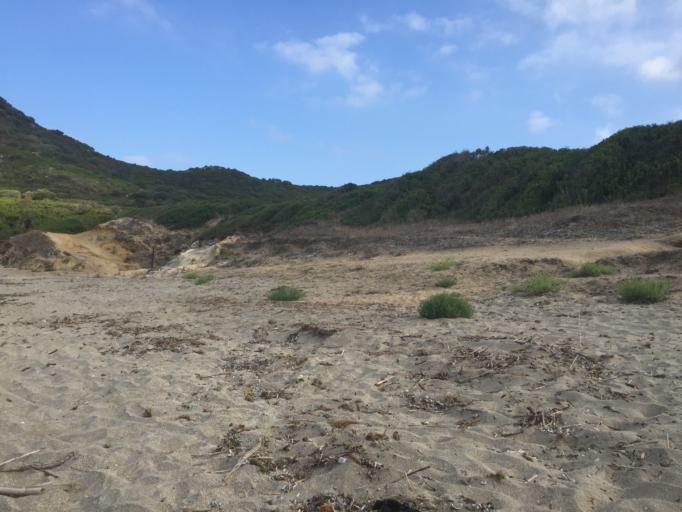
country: IT
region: Sardinia
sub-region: Provincia di Cagliari
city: Olia Speciosa
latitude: 39.3114
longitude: 9.6128
